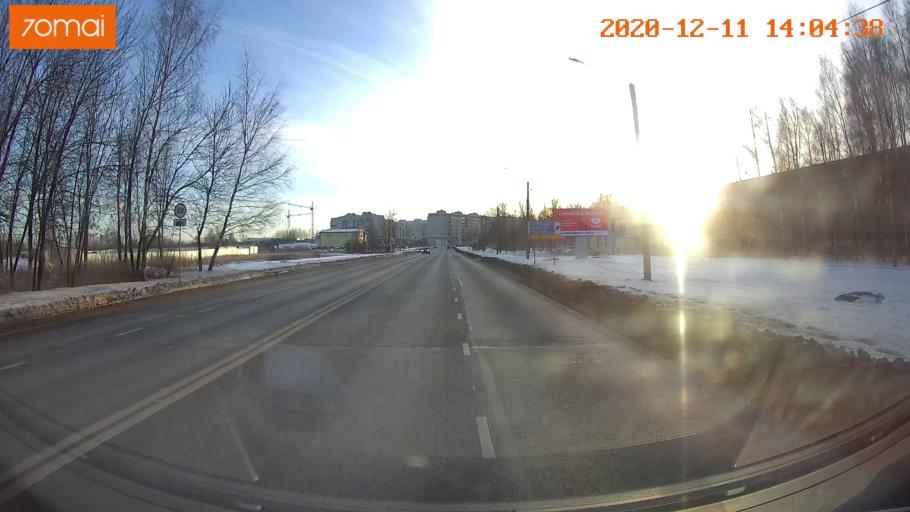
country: RU
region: Kostroma
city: Oktyabr'skiy
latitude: 57.7535
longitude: 41.0164
